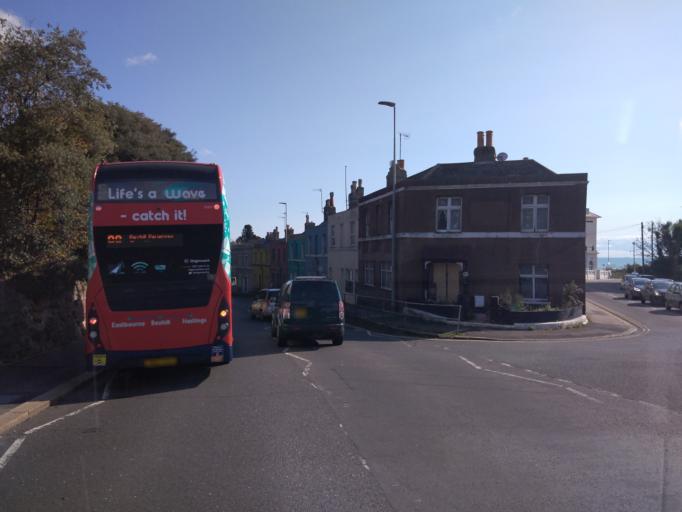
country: GB
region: England
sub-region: East Sussex
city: Hastings
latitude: 50.8552
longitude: 0.5725
